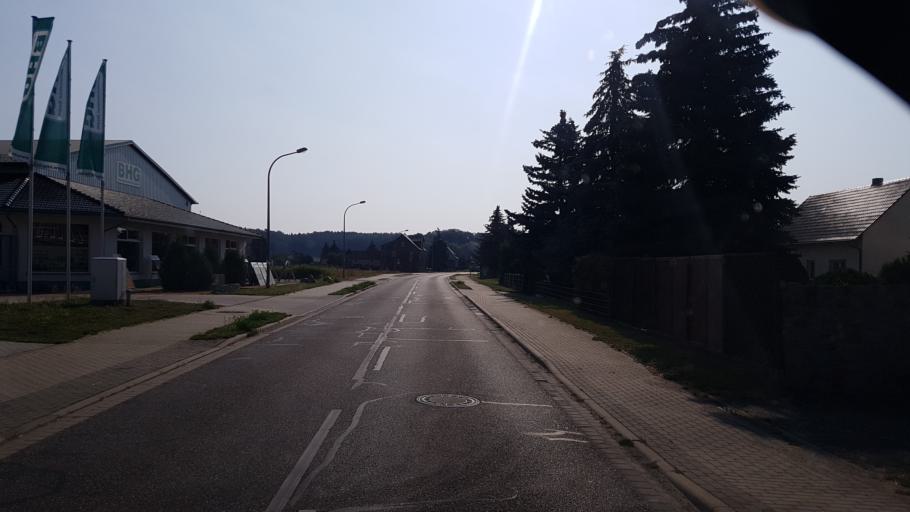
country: DE
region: Brandenburg
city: Drebkau
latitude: 51.6950
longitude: 14.2568
